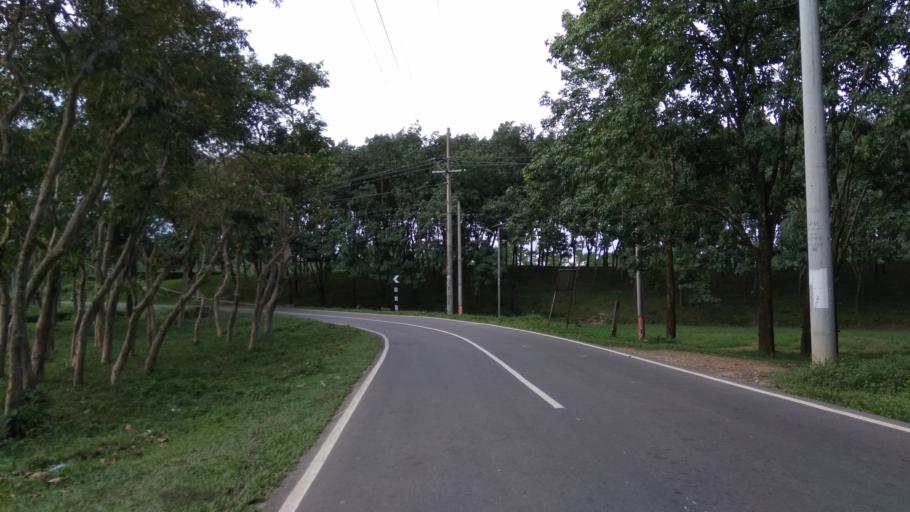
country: IN
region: Tripura
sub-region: Dhalai
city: Kamalpur
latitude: 24.3014
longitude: 91.7541
